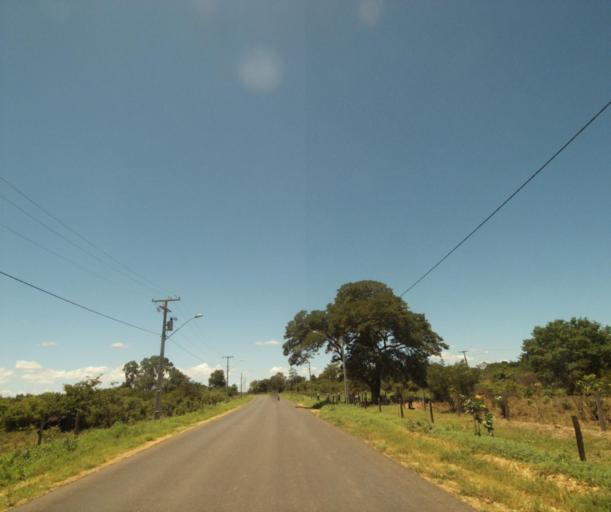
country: BR
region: Bahia
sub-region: Carinhanha
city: Carinhanha
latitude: -14.3155
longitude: -43.7779
